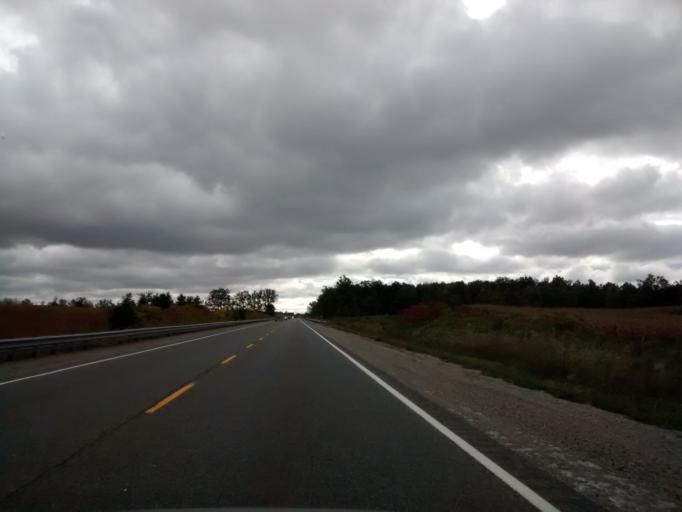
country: CA
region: Ontario
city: Ancaster
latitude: 43.1592
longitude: -79.9501
